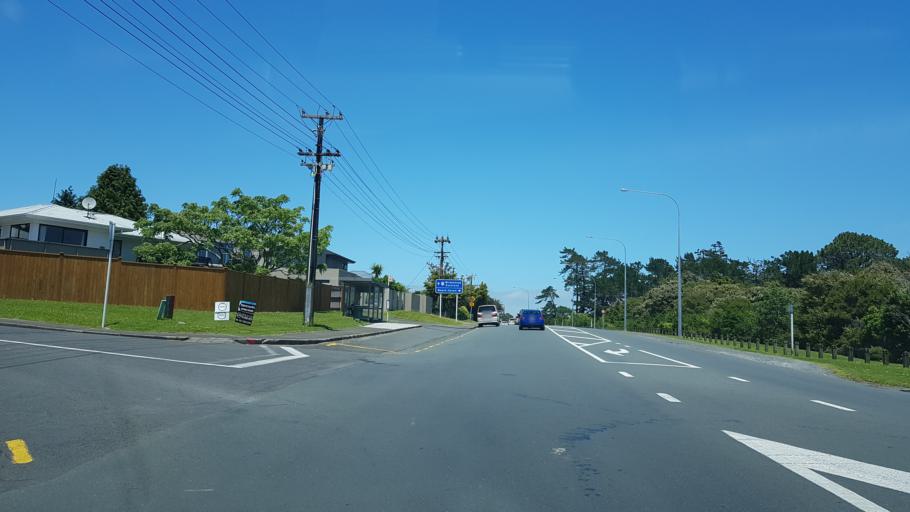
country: NZ
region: Auckland
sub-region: Auckland
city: North Shore
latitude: -36.7961
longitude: 174.7237
